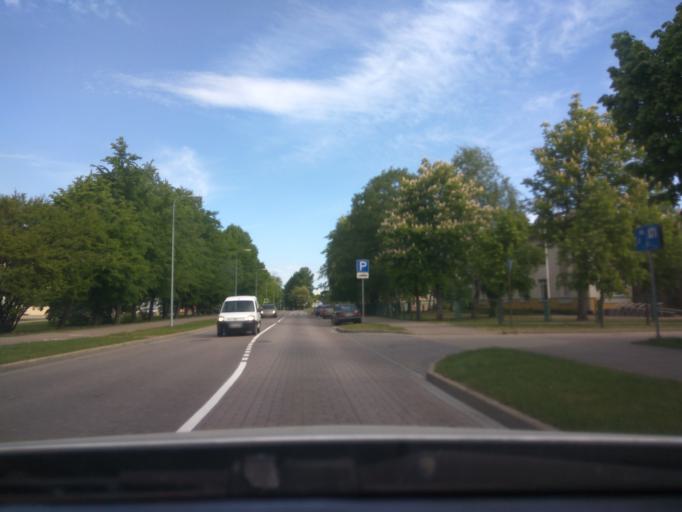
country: LV
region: Ventspils
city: Ventspils
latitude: 57.3930
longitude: 21.5734
